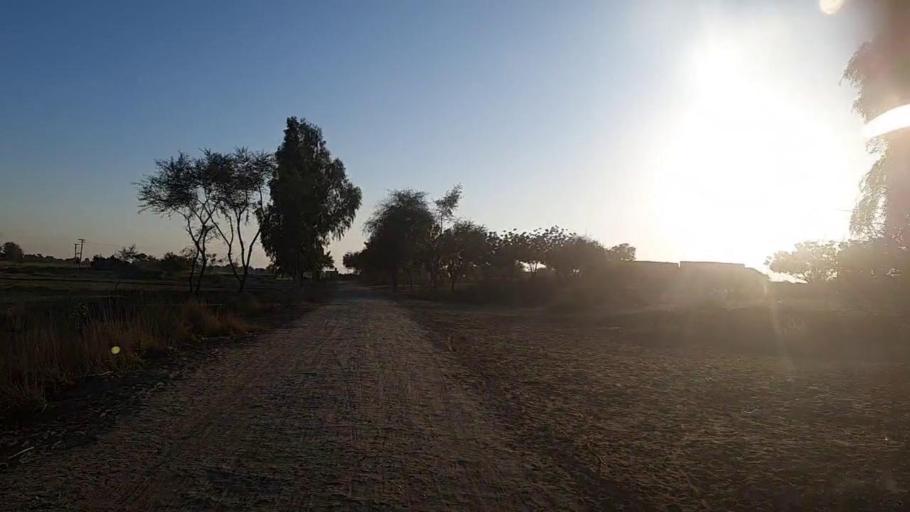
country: PK
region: Sindh
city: Khairpur
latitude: 27.9094
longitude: 69.6811
